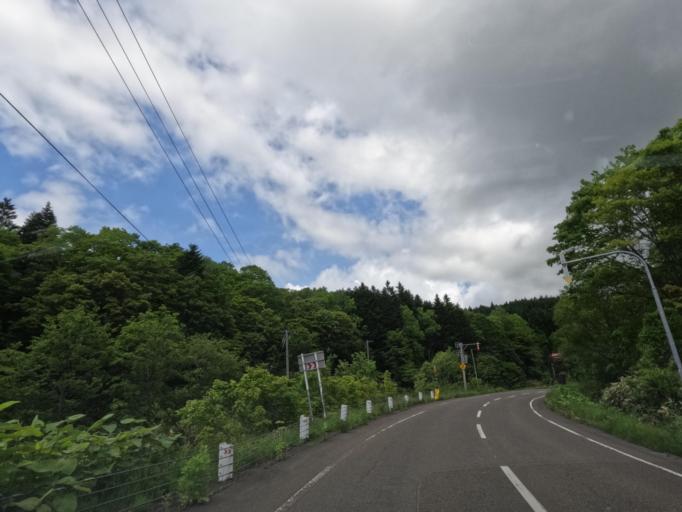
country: JP
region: Hokkaido
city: Tobetsu
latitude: 43.4804
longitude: 141.5964
